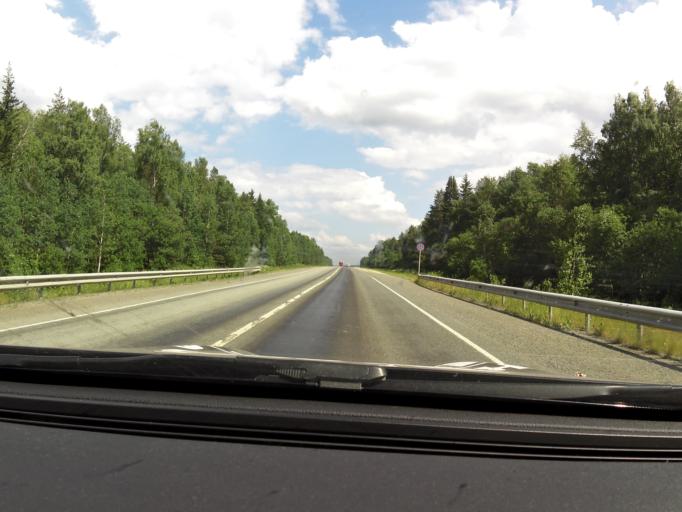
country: RU
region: Sverdlovsk
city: Bisert'
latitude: 56.8335
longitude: 58.9397
